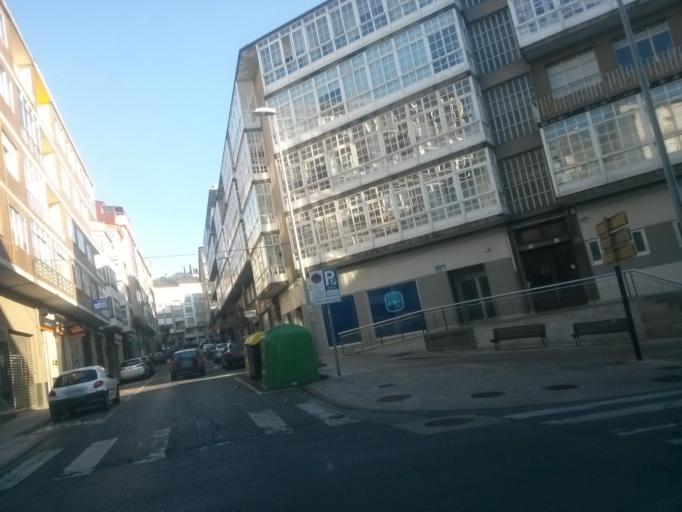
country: ES
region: Galicia
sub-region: Provincia de Lugo
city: Lugo
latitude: 43.0138
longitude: -7.5643
